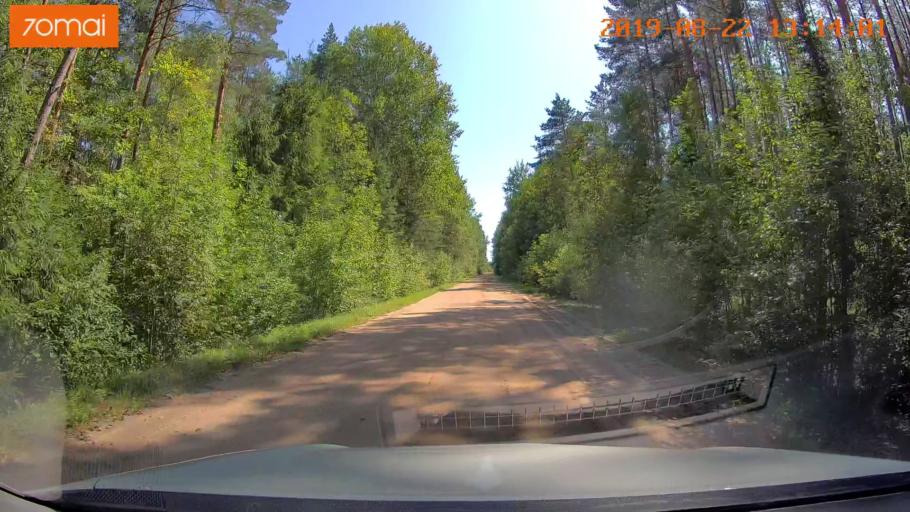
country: BY
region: Minsk
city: Prawdzinski
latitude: 53.2715
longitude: 27.8826
